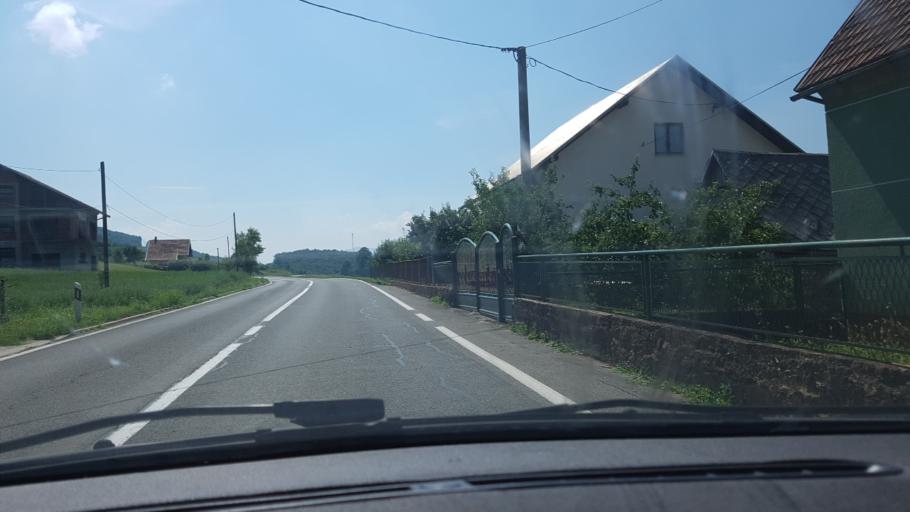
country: HR
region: Licko-Senjska
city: Otocac
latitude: 44.8865
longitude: 15.1937
